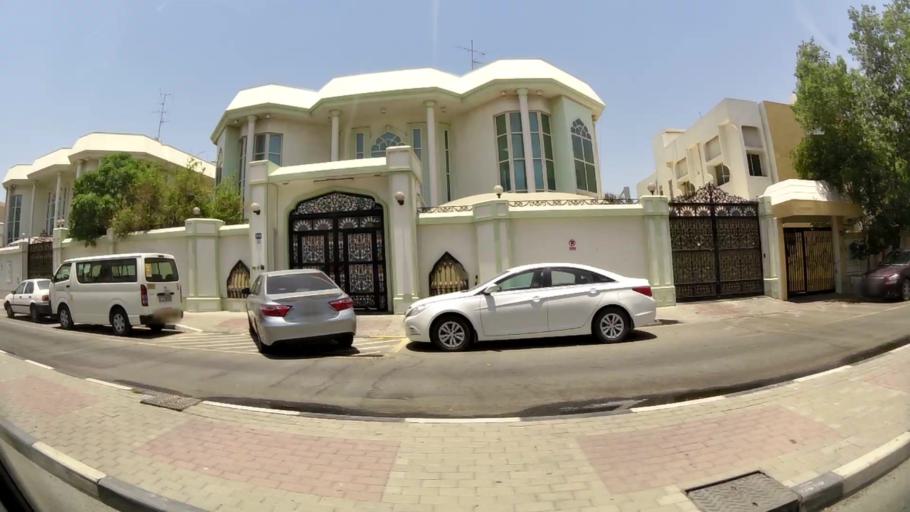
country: AE
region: Ash Shariqah
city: Sharjah
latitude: 25.2782
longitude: 55.3237
